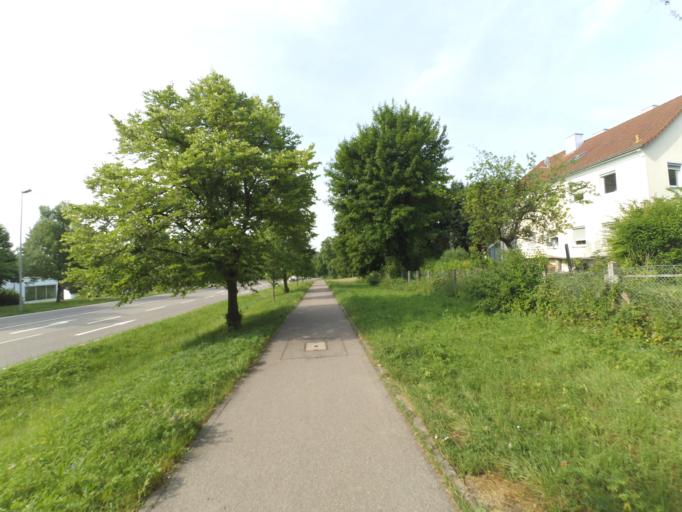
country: DE
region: Baden-Wuerttemberg
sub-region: Tuebingen Region
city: Ulm
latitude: 48.4218
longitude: 10.0048
